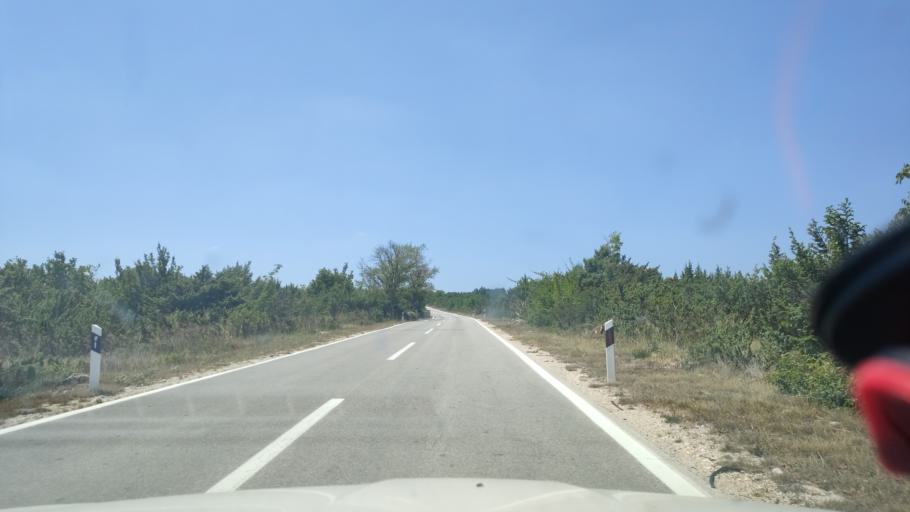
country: HR
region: Sibensko-Kniniska
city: Kistanje
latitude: 44.0083
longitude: 16.0042
